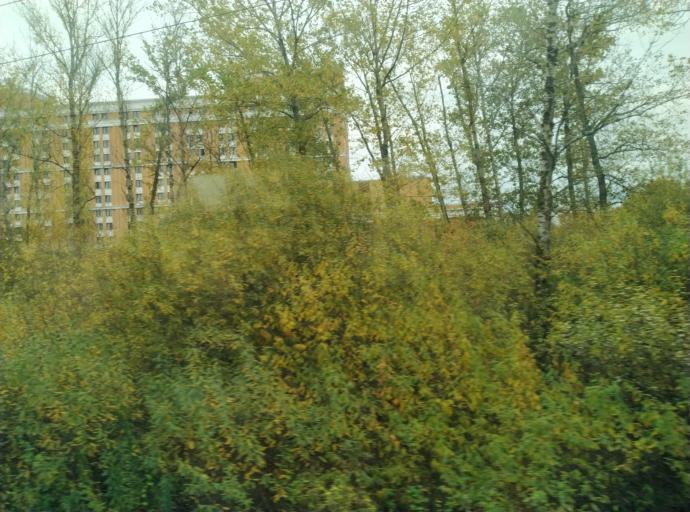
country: RU
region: Moskovskaya
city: Bol'shiye Vyazemy
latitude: 55.6264
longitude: 36.9760
